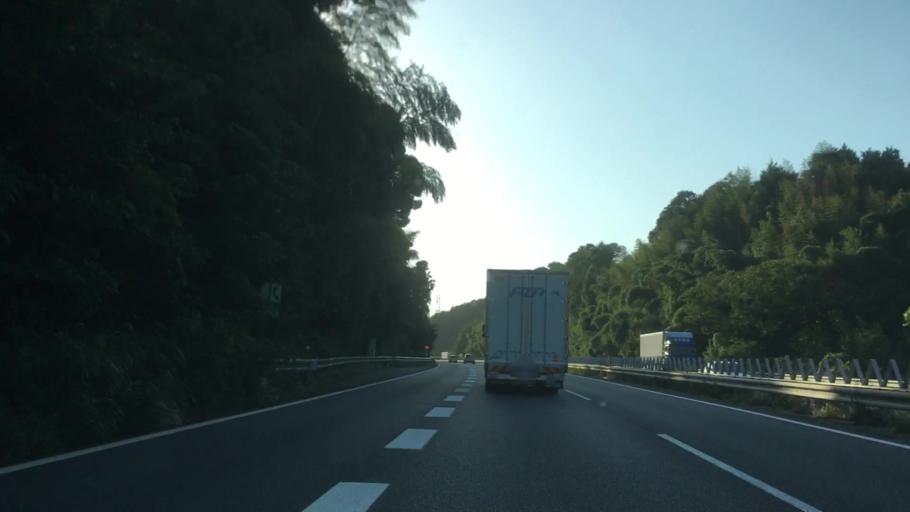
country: JP
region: Yamaguchi
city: Onoda
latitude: 34.1173
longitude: 131.1159
